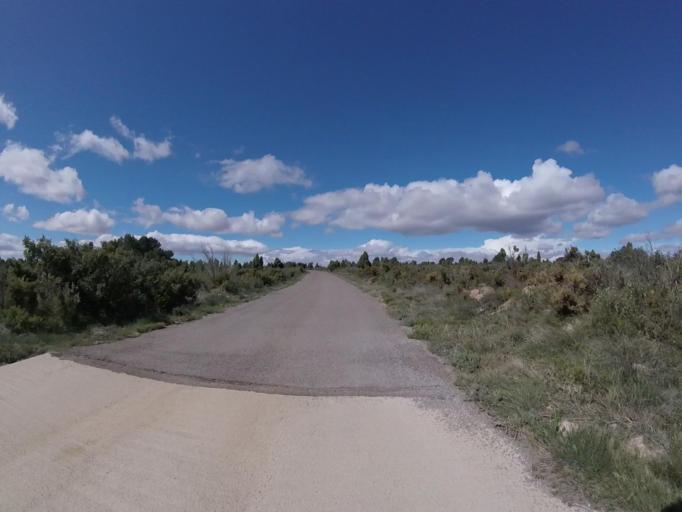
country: ES
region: Valencia
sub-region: Provincia de Castello
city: Culla
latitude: 40.3065
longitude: -0.1068
